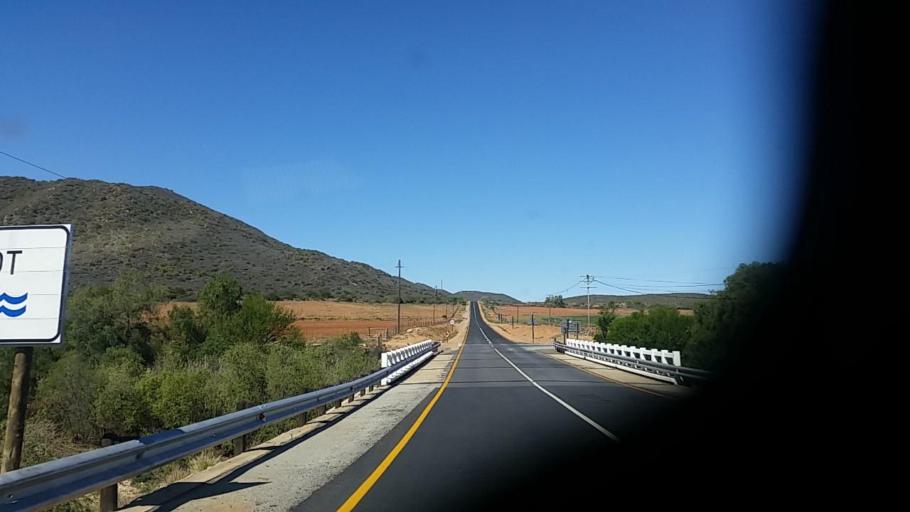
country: ZA
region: Western Cape
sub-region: Eden District Municipality
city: Oudtshoorn
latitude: -33.4865
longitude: 22.5433
